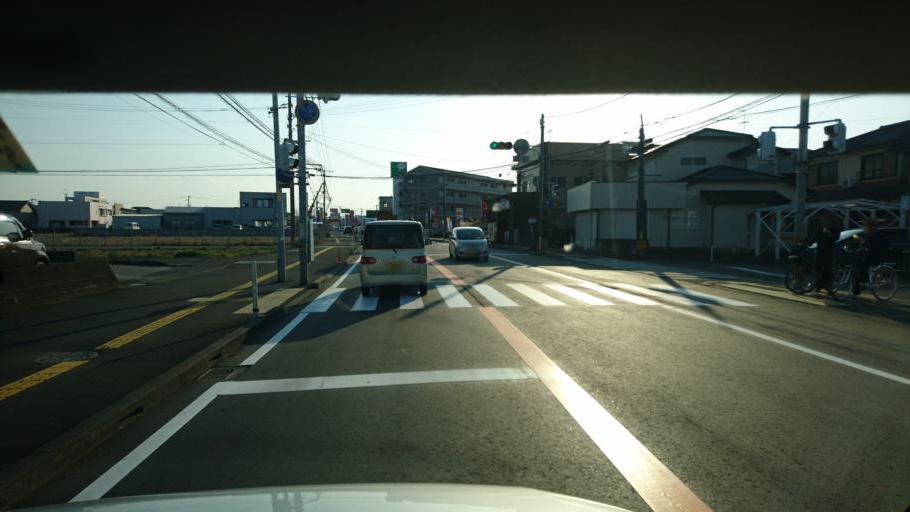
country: JP
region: Miyazaki
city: Miyazaki-shi
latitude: 31.9880
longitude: 131.4519
